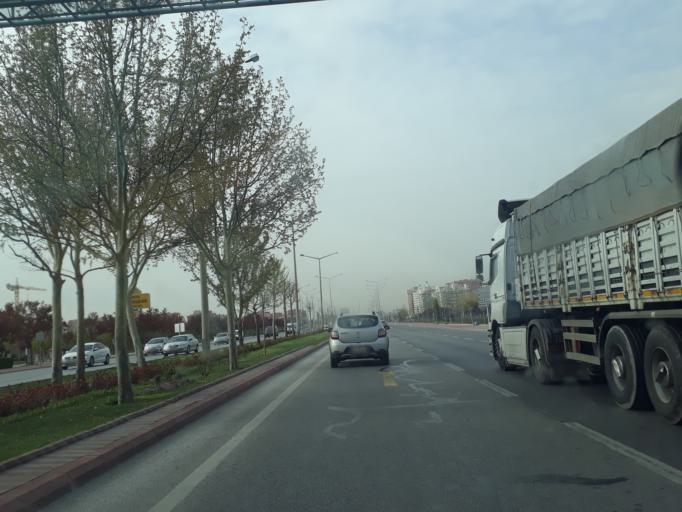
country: TR
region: Konya
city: Selcuklu
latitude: 37.9631
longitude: 32.5146
